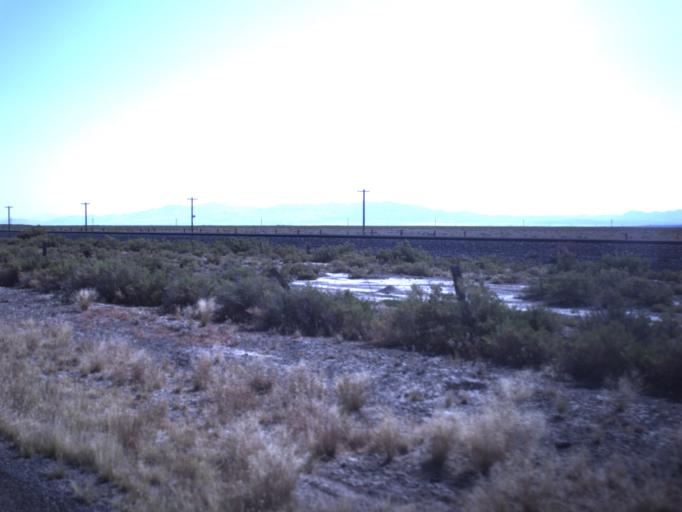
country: US
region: Utah
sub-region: Millard County
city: Delta
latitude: 39.1319
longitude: -112.7307
